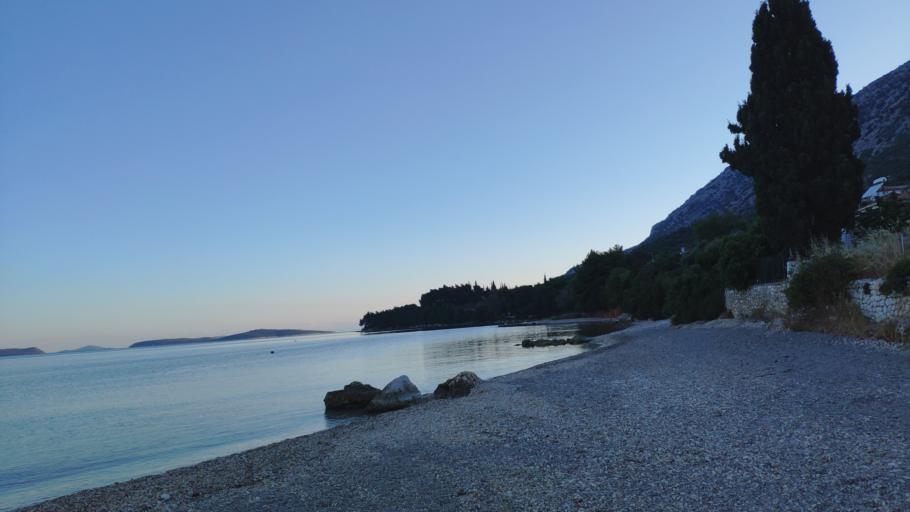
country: GR
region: West Greece
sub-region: Nomos Aitolias kai Akarnanias
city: Astakos
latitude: 38.5291
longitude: 21.0748
